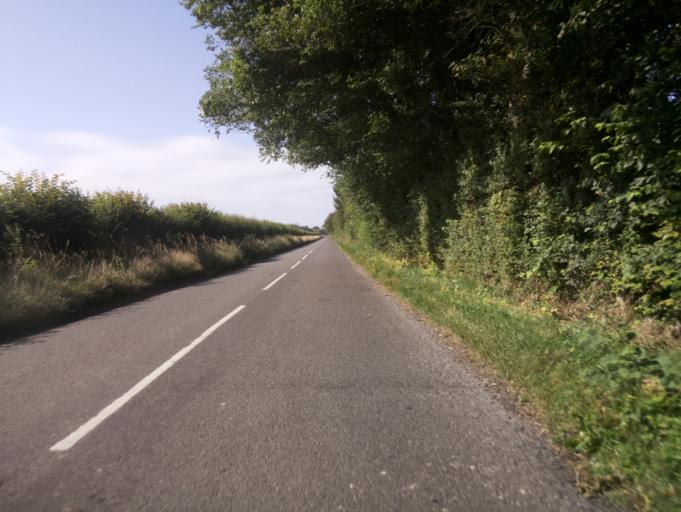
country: GB
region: England
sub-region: Oxfordshire
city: Ducklington
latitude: 51.7349
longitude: -1.5034
